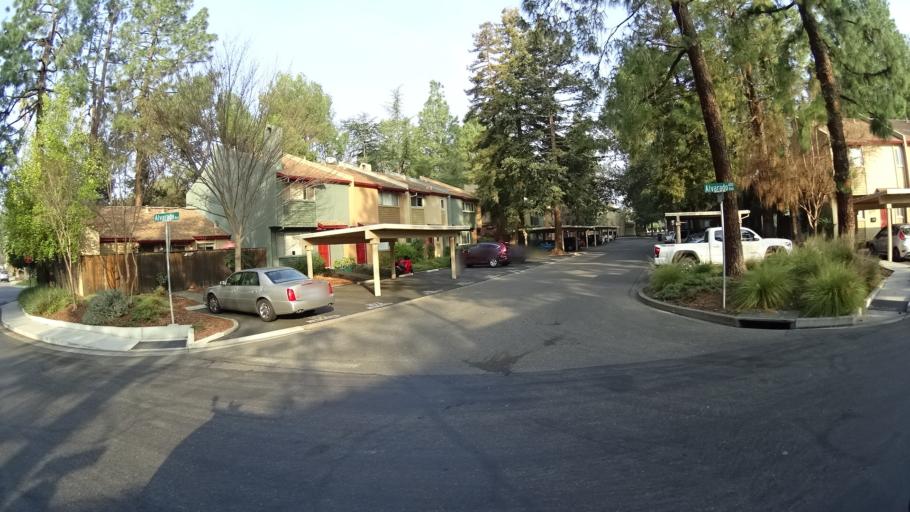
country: US
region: California
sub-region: Yolo County
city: Davis
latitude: 38.5618
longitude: -121.7499
